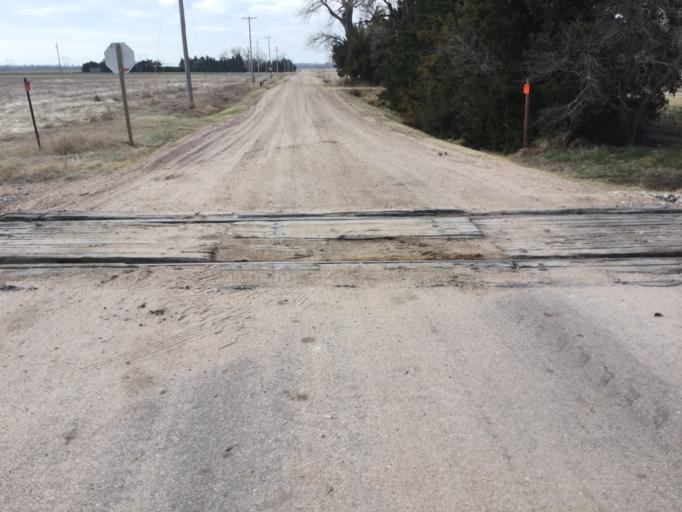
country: US
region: Kansas
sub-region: Barton County
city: Ellinwood
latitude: 38.3642
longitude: -98.6455
